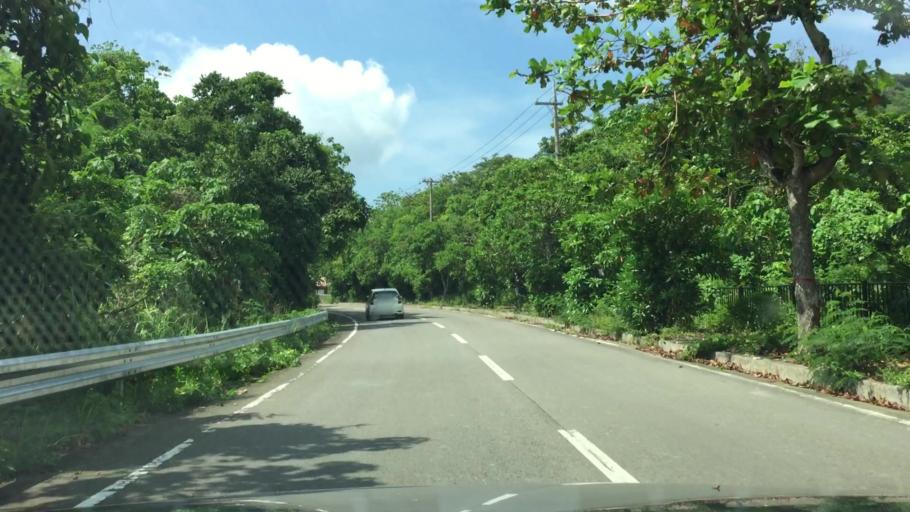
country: JP
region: Okinawa
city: Ishigaki
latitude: 24.4680
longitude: 124.2256
